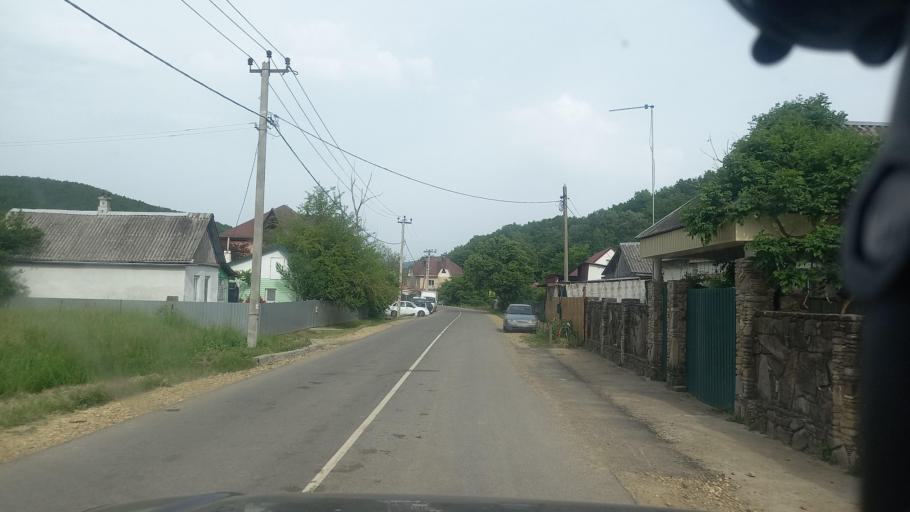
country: RU
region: Krasnodarskiy
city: Goryachiy Klyuch
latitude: 44.6054
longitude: 38.9940
